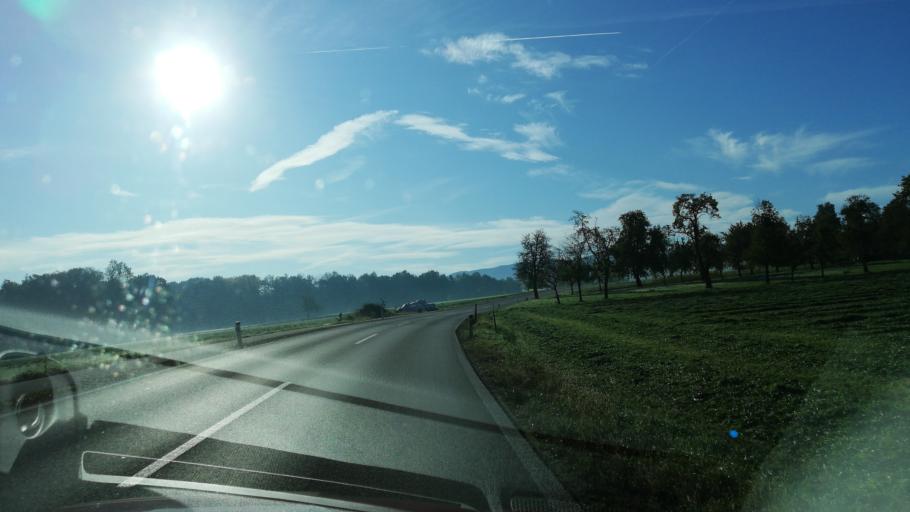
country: AT
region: Upper Austria
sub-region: Politischer Bezirk Steyr-Land
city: Waldneukirchen
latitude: 48.0159
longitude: 14.2411
